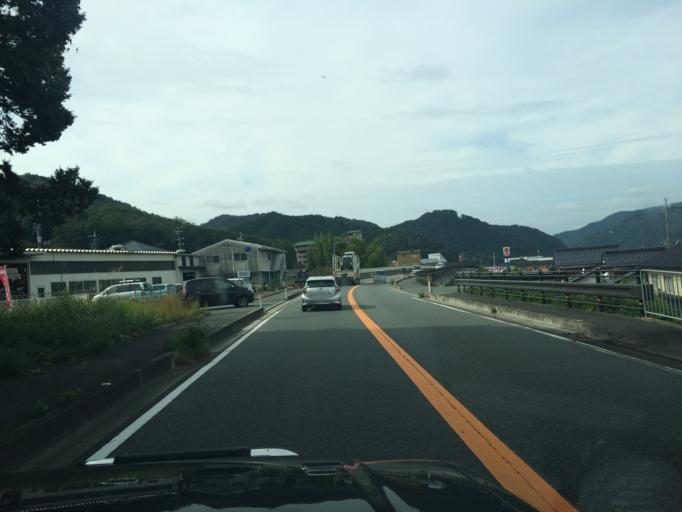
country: JP
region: Hyogo
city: Toyooka
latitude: 35.3396
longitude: 134.8444
